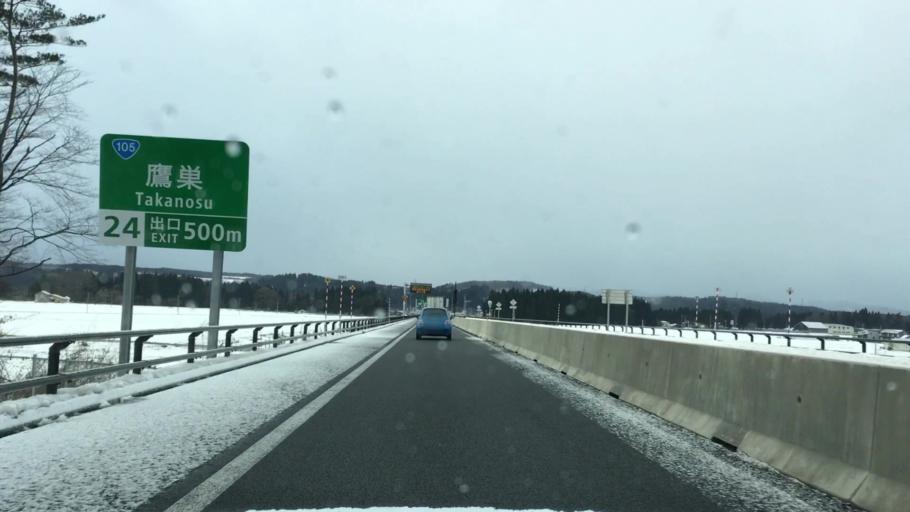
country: JP
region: Akita
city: Takanosu
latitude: 40.2058
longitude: 140.4046
